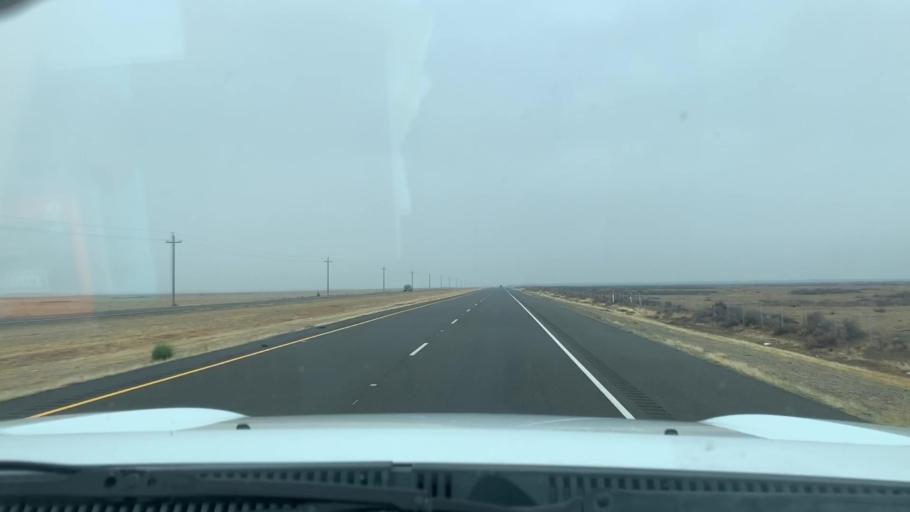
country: US
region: California
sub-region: Kern County
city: Lost Hills
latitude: 35.6156
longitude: -119.7884
